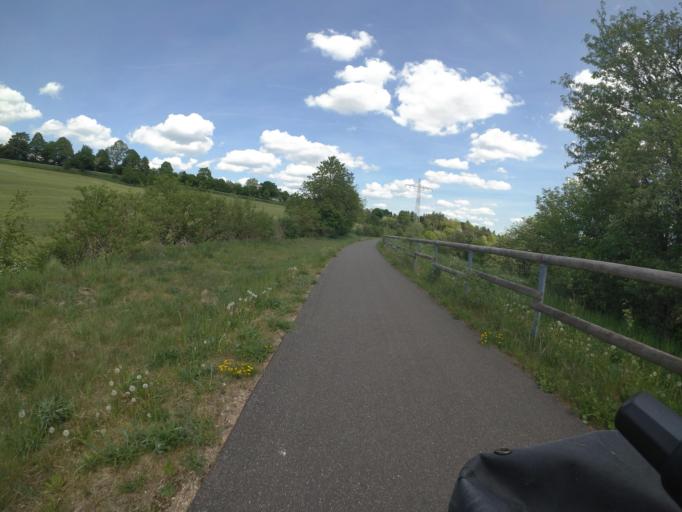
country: DE
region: Rheinland-Pfalz
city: Scheid
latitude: 50.3538
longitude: 6.4237
